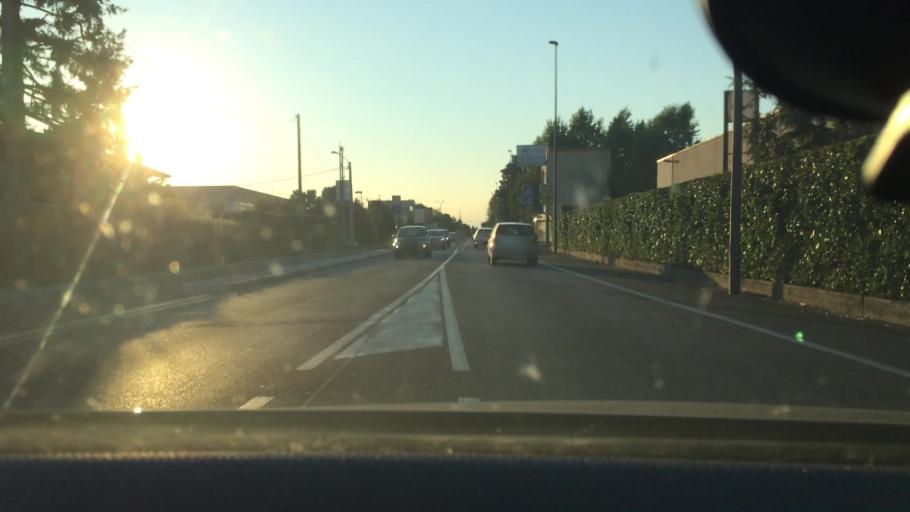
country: IT
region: Lombardy
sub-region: Provincia di Varese
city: Gerenzano
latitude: 45.6453
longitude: 8.9973
